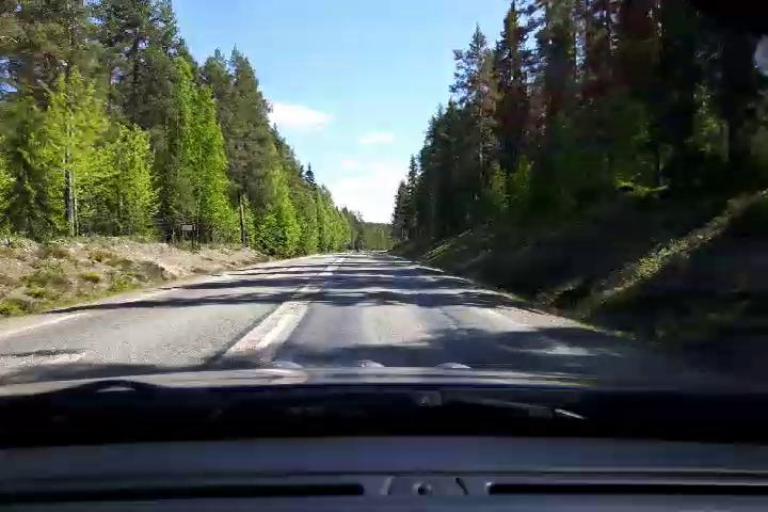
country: SE
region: Gaevleborg
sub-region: Ljusdals Kommun
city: Farila
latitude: 61.9741
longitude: 15.3382
